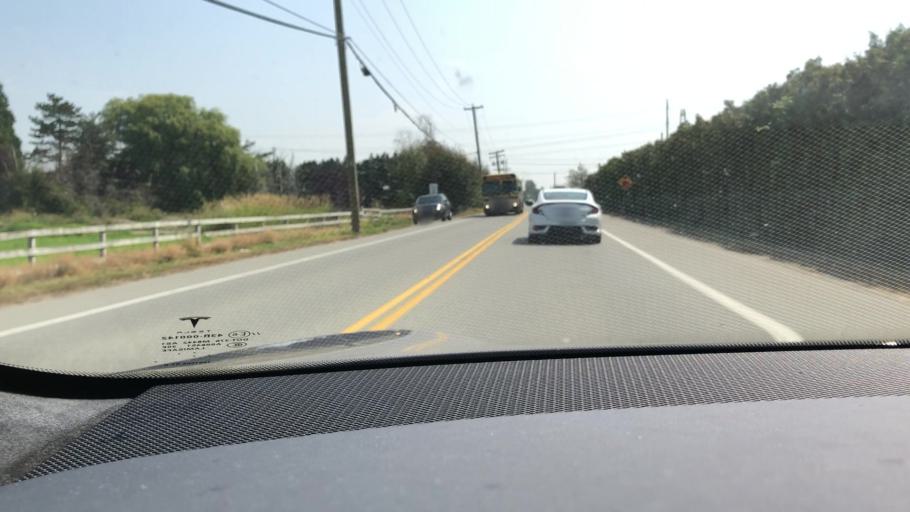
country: CA
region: British Columbia
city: Ladner
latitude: 49.0539
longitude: -123.0794
